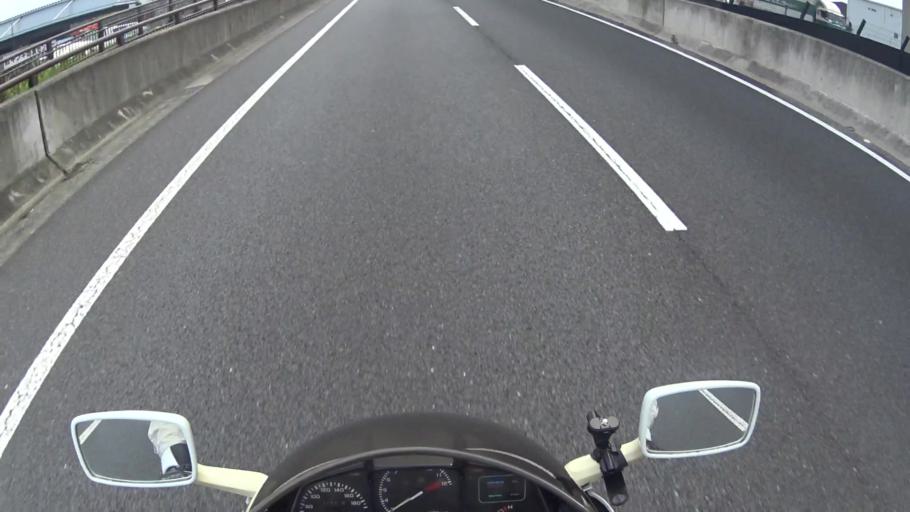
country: JP
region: Kyoto
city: Muko
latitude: 34.9253
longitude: 135.7507
